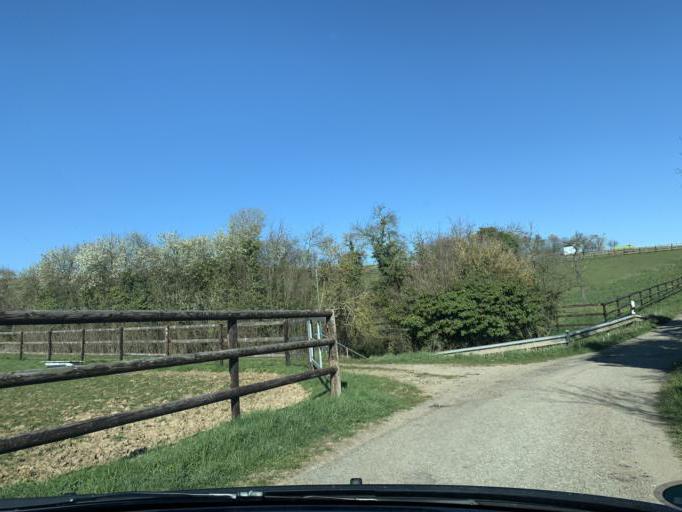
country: DE
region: North Rhine-Westphalia
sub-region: Regierungsbezirk Koln
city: Nideggen
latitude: 50.7041
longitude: 6.5191
